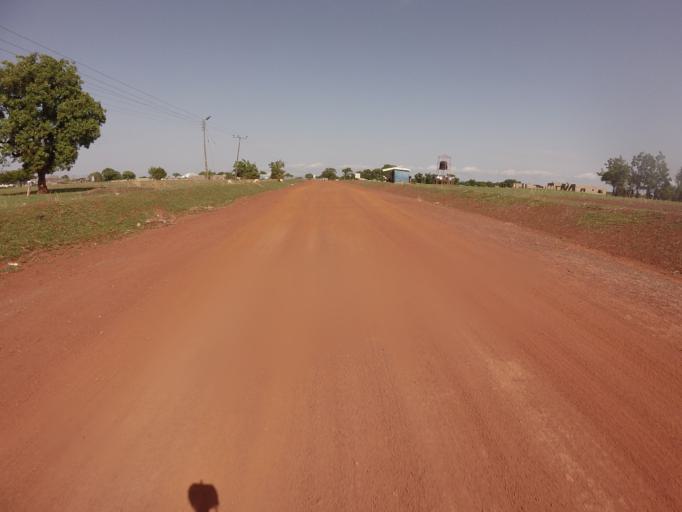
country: GH
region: Upper East
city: Bawku
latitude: 10.8332
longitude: -0.1729
